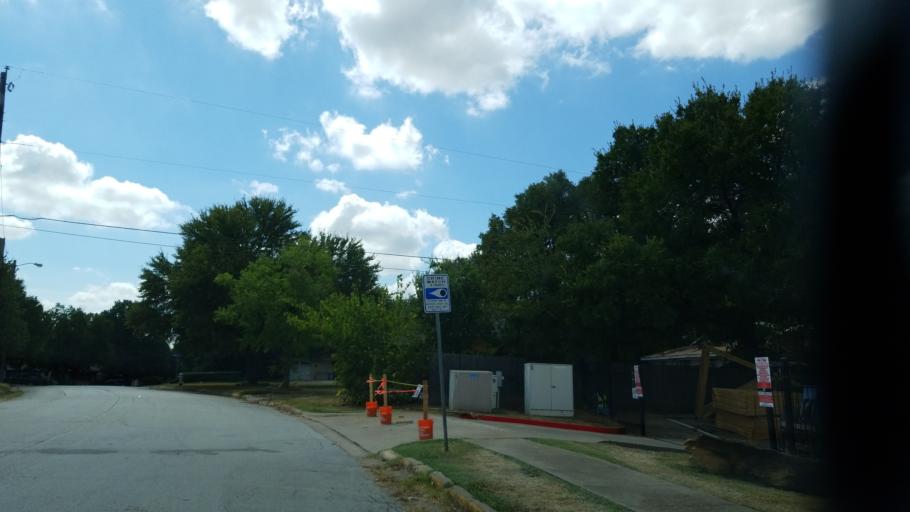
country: US
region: Texas
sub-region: Tarrant County
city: Euless
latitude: 32.8337
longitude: -97.0875
